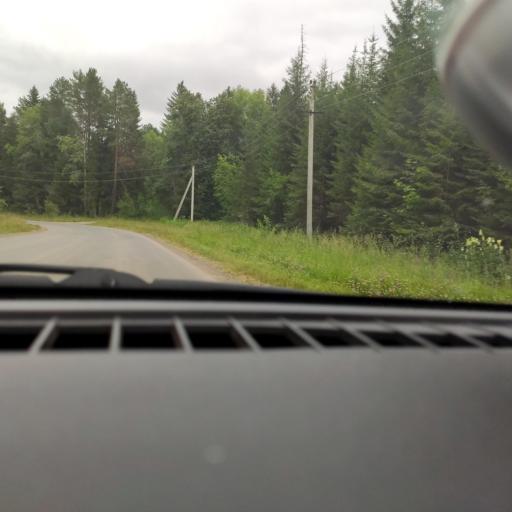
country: RU
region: Perm
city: Polazna
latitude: 58.3410
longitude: 56.2357
